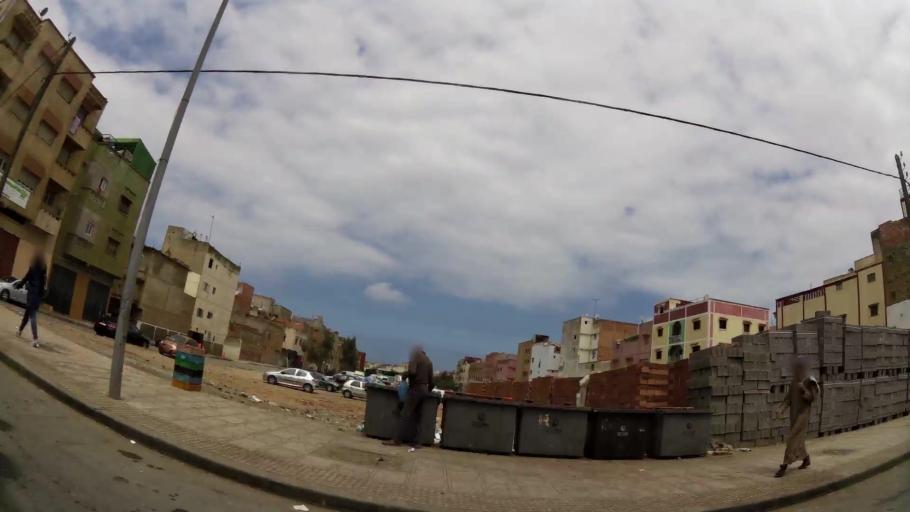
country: MA
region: Rabat-Sale-Zemmour-Zaer
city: Sale
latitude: 34.0552
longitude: -6.7792
